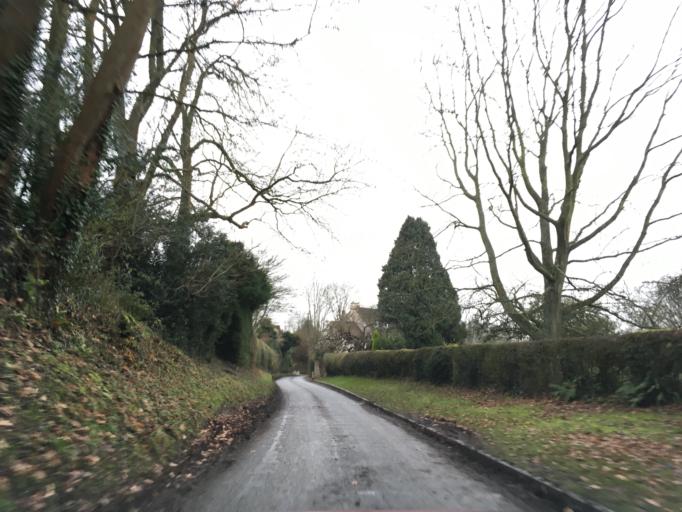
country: GB
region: England
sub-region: Gloucestershire
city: Wotton-under-Edge
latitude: 51.6168
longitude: -2.3314
